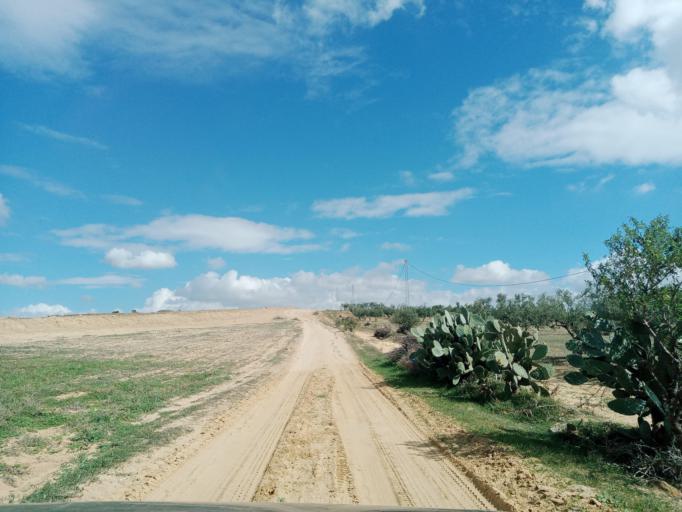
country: TN
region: Tunis
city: Oued Lill
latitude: 36.8070
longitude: 9.9864
